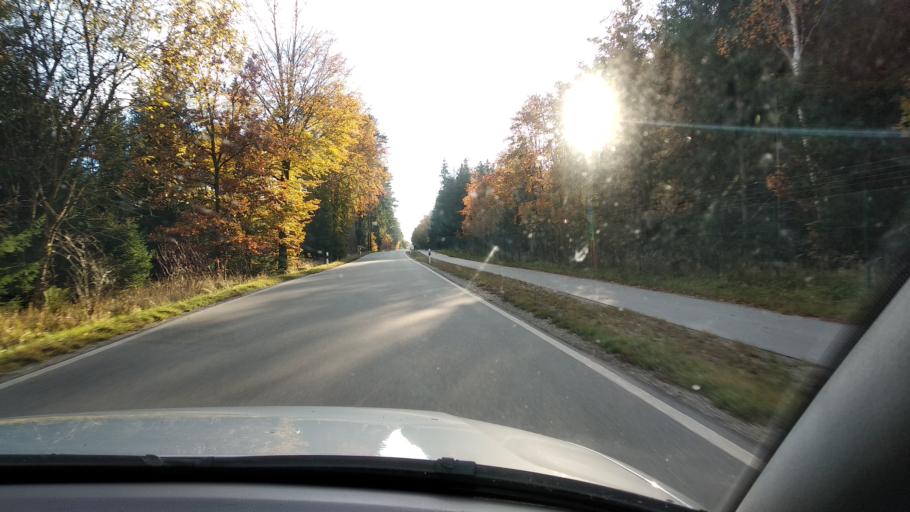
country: DE
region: Bavaria
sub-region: Upper Bavaria
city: Hohenkirchen-Siegertsbrunn
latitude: 48.0359
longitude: 11.7452
